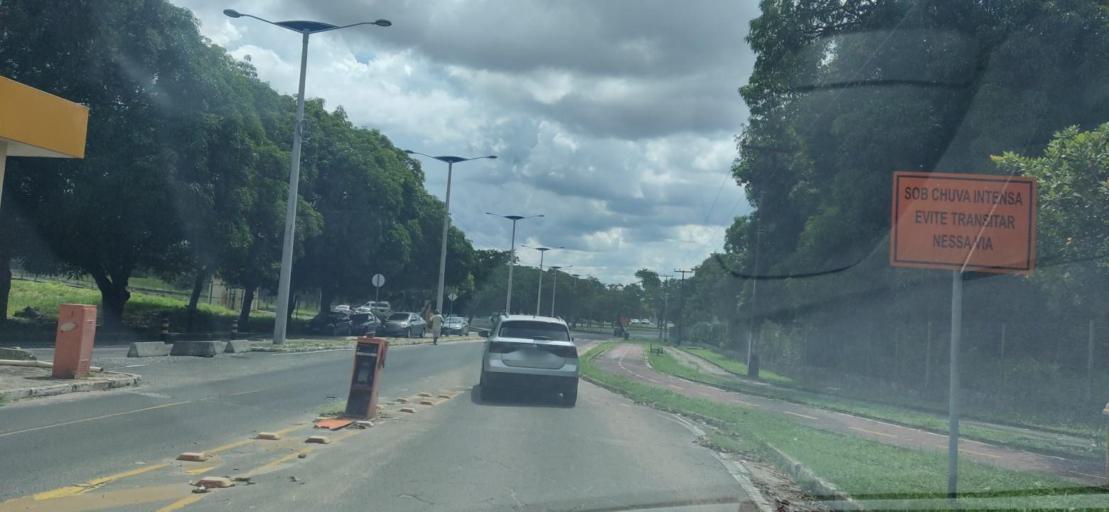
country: BR
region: Piaui
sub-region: Teresina
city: Teresina
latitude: -5.0581
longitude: -42.7931
